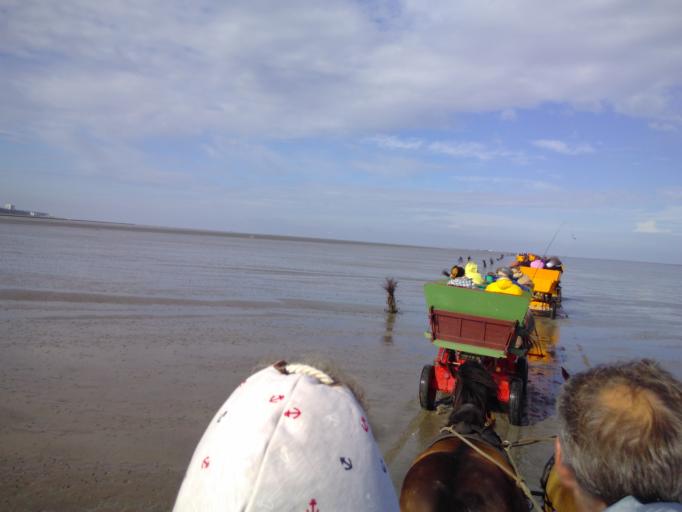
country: DE
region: Lower Saxony
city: Cuxhaven
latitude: 53.8889
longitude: 8.6200
